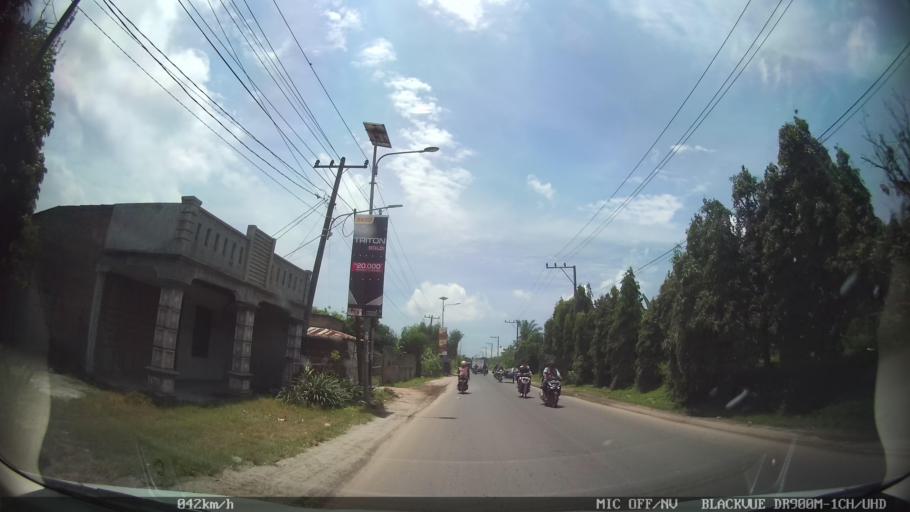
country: ID
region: North Sumatra
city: Perbaungan
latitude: 3.5291
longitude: 98.8874
